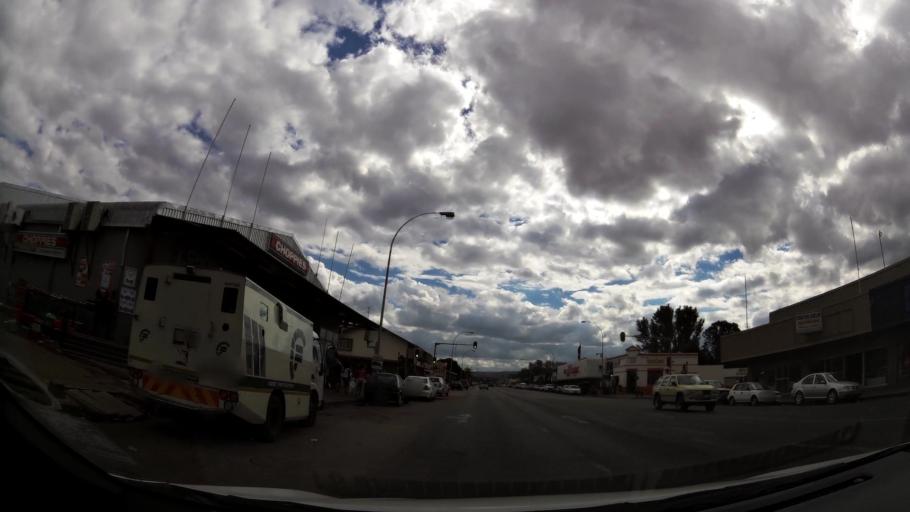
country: ZA
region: Limpopo
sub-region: Waterberg District Municipality
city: Modimolle
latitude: -24.7051
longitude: 28.4104
